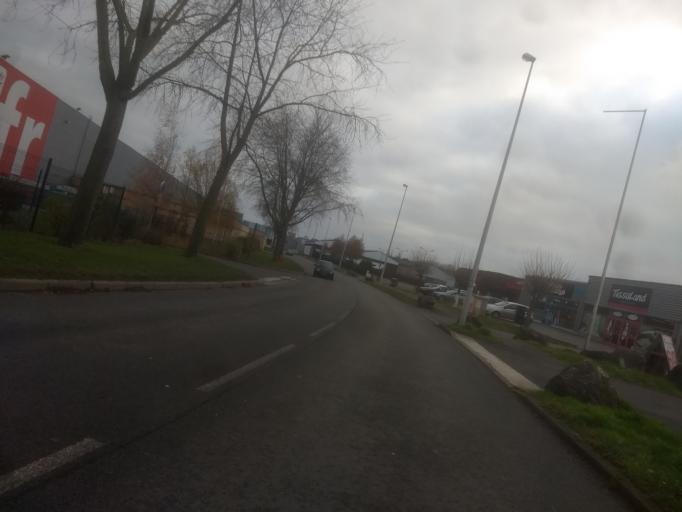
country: FR
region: Nord-Pas-de-Calais
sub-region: Departement du Pas-de-Calais
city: Dainville
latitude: 50.2997
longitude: 2.7287
